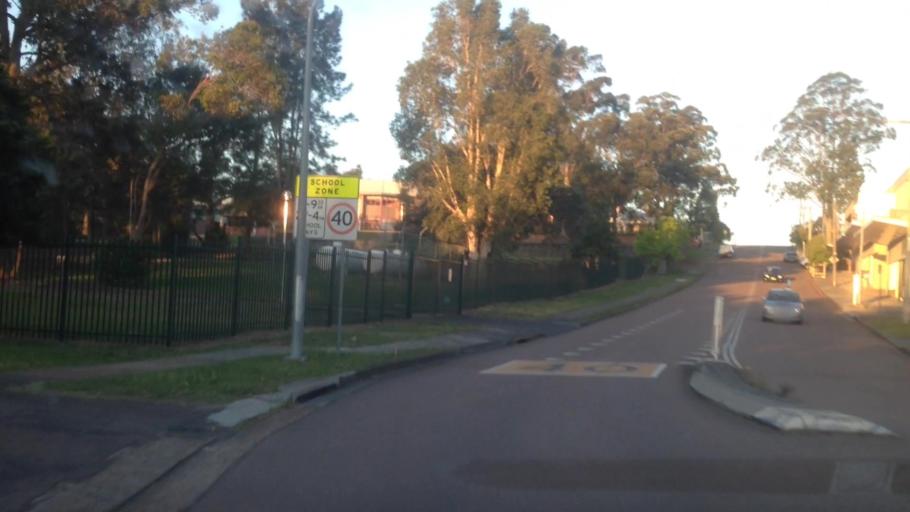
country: AU
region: New South Wales
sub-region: Lake Macquarie Shire
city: Dora Creek
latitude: -33.1067
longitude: 151.4867
